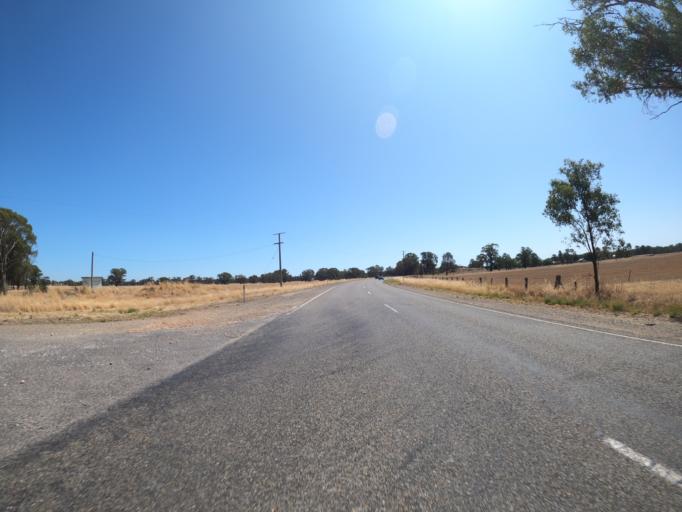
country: AU
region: New South Wales
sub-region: Corowa Shire
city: Corowa
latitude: -36.0839
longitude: 146.3326
